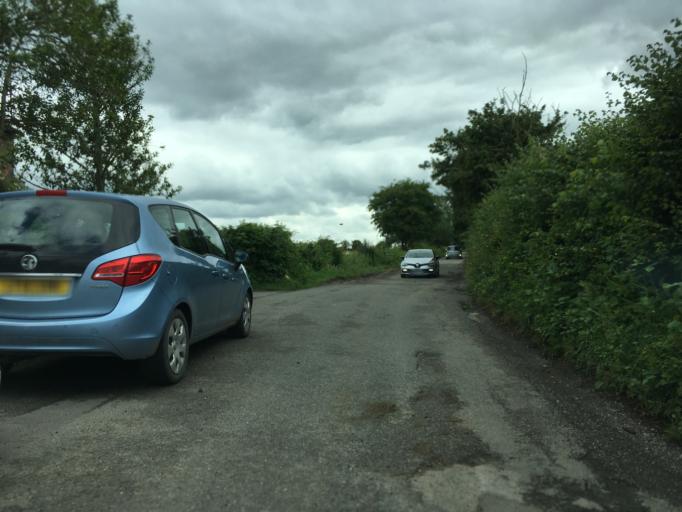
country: GB
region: England
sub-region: Gloucestershire
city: Stonehouse
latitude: 51.7914
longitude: -2.3727
